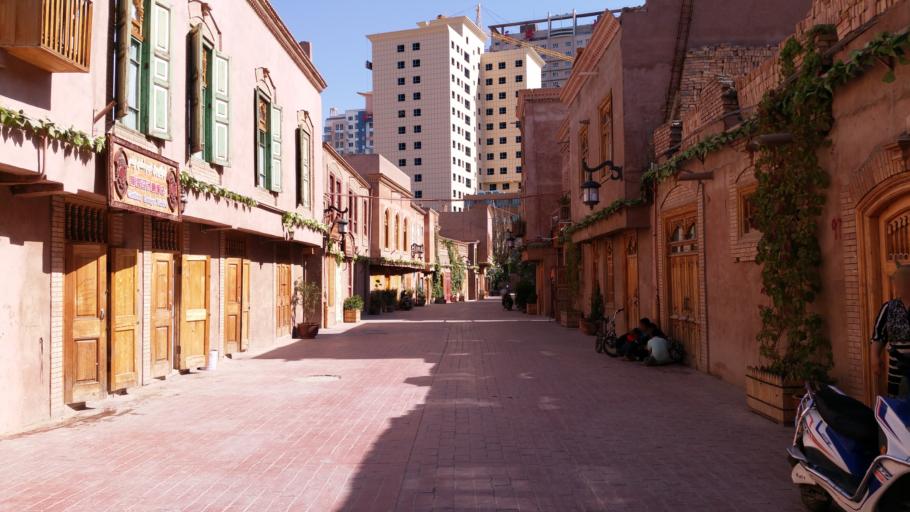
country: CN
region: Xinjiang Uygur Zizhiqu
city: Kashi
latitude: 39.4686
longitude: 75.9811
